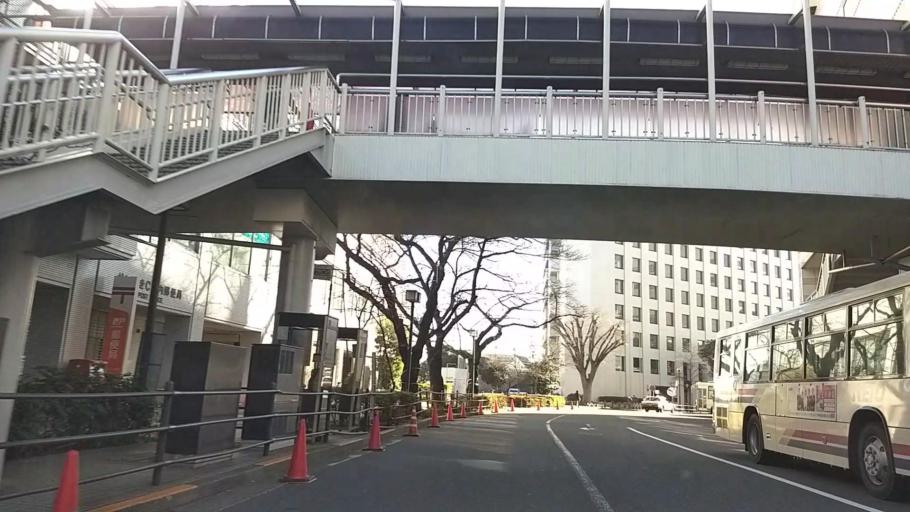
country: JP
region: Tokyo
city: Hino
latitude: 35.6518
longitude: 139.4471
